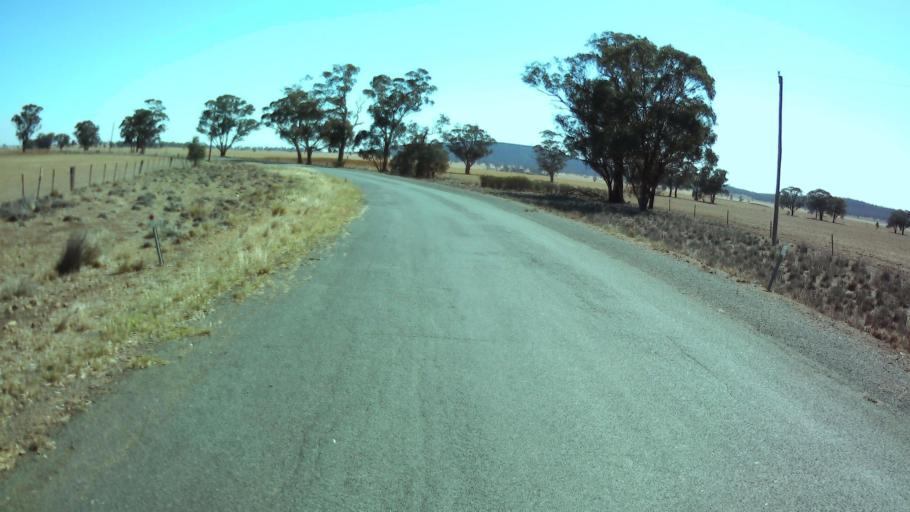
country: AU
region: New South Wales
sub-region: Weddin
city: Grenfell
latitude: -33.7056
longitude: 147.9175
